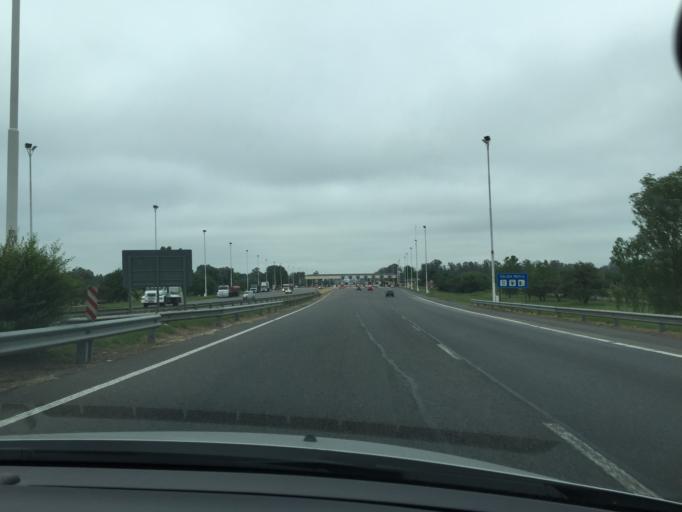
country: AR
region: Buenos Aires
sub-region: Partido de Ezeiza
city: Ezeiza
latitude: -34.8521
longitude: -58.5479
